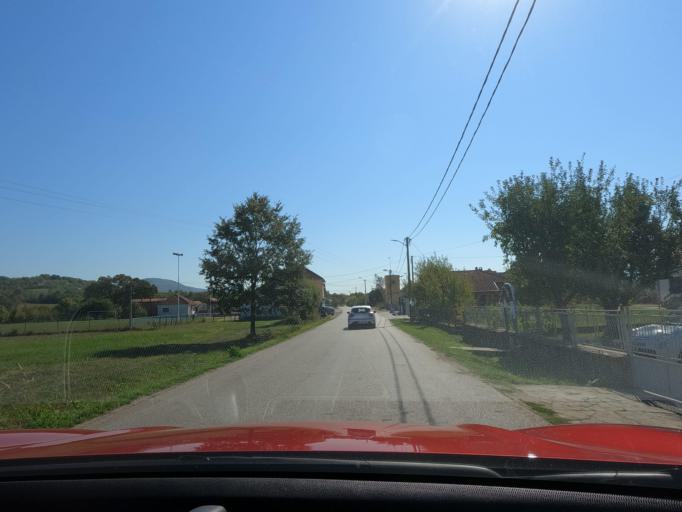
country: RS
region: Central Serbia
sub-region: Raski Okrug
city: Kraljevo
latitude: 43.7621
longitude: 20.6766
